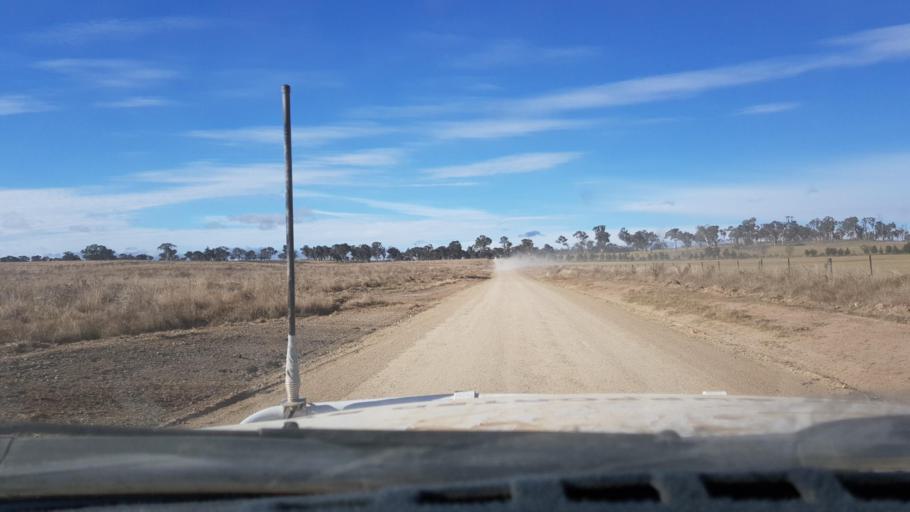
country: AU
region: New South Wales
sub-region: Armidale Dumaresq
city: Armidale
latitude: -30.7052
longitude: 151.5870
